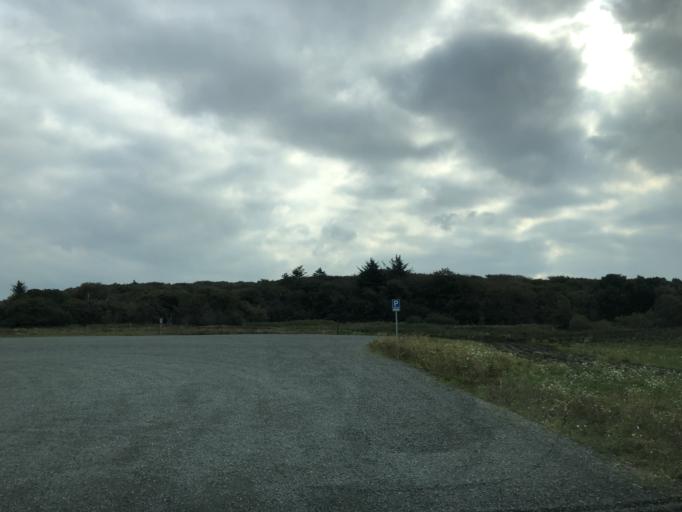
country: DK
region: Central Jutland
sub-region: Ringkobing-Skjern Kommune
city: Ringkobing
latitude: 56.1021
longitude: 8.2471
